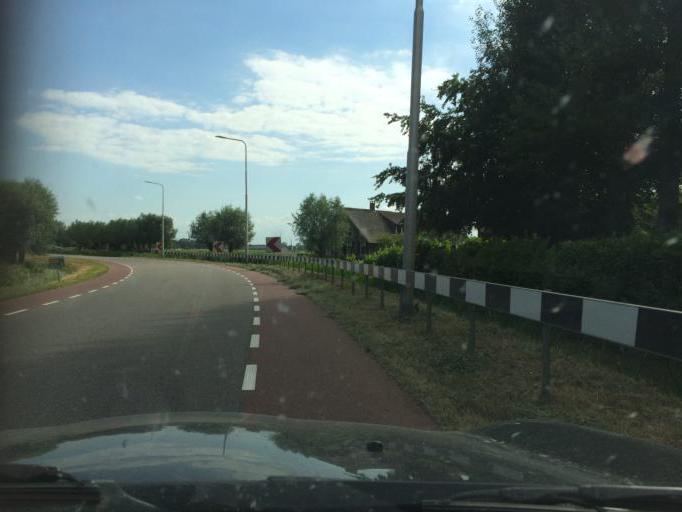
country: NL
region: Utrecht
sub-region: Gemeente Woerden
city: Woerden
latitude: 52.1074
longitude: 4.8948
